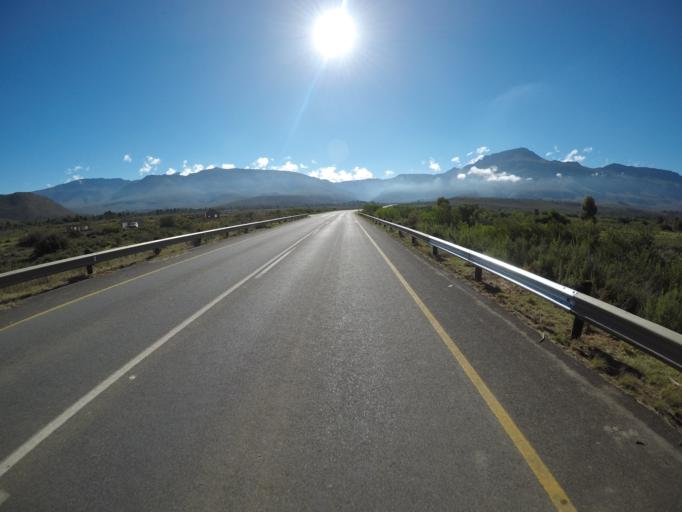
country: ZA
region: Western Cape
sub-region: Overberg District Municipality
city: Caledon
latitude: -34.0636
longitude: 19.5583
